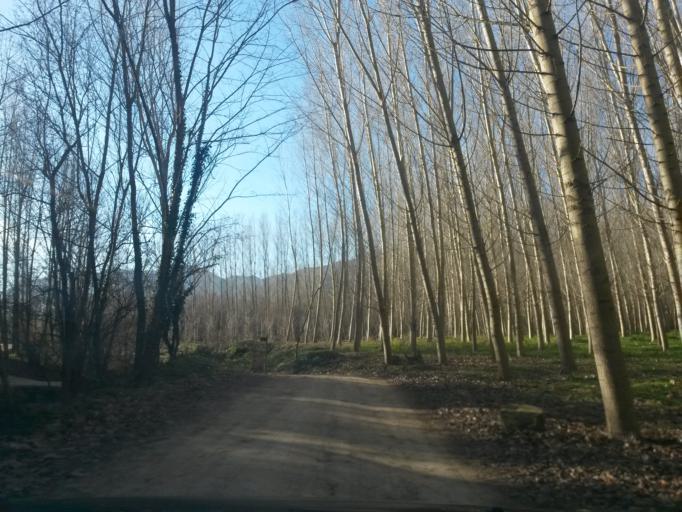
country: ES
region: Catalonia
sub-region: Provincia de Girona
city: la Cellera de Ter
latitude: 41.9875
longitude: 2.6247
